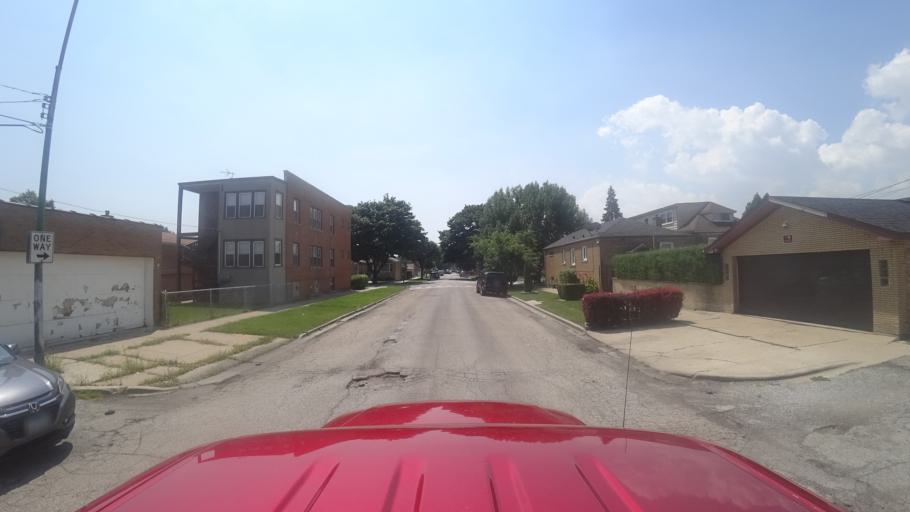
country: US
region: Illinois
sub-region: Cook County
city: Hometown
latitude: 41.7874
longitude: -87.7206
